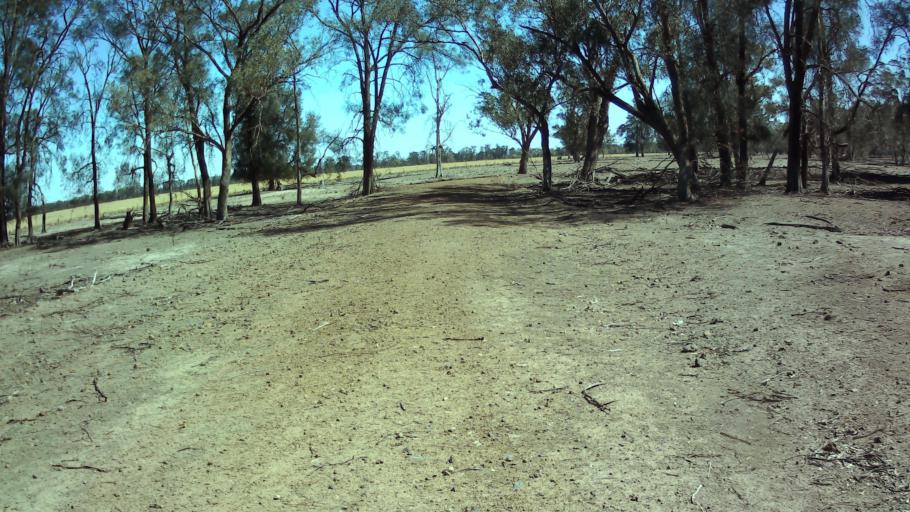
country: AU
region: New South Wales
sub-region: Bland
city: West Wyalong
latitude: -33.7689
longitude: 147.6571
